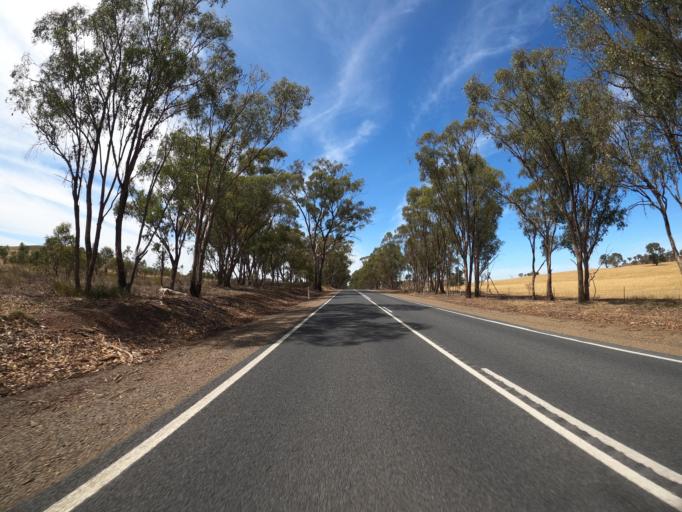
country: AU
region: Victoria
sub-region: Benalla
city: Benalla
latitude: -36.3724
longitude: 145.9732
